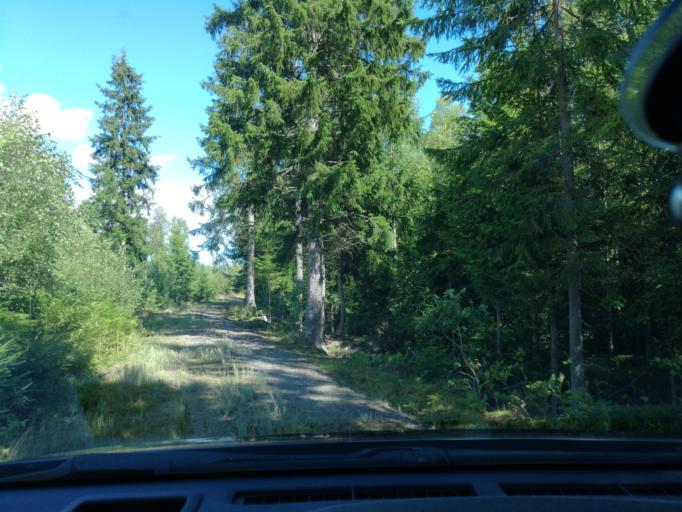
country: SE
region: Kronoberg
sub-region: Alvesta Kommun
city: Vislanda
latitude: 56.7057
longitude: 14.4018
